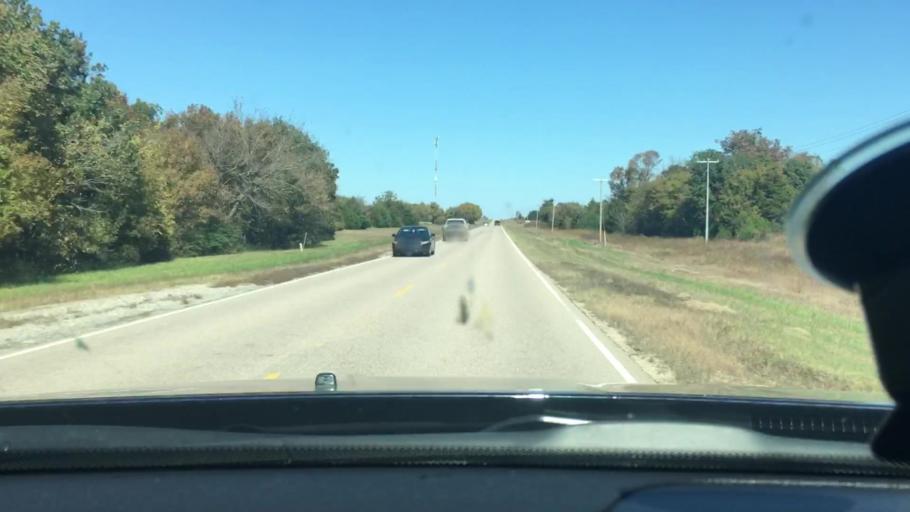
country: US
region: Oklahoma
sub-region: Johnston County
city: Tishomingo
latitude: 34.4230
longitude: -96.6359
